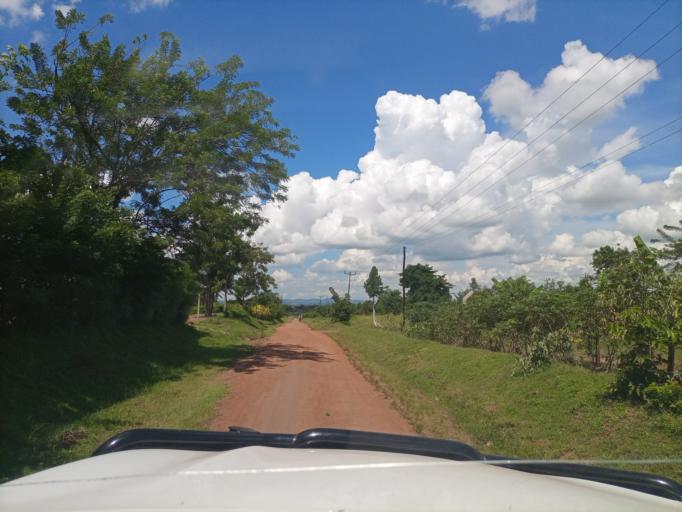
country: UG
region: Eastern Region
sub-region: Tororo District
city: Tororo
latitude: 0.6892
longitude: 34.0096
